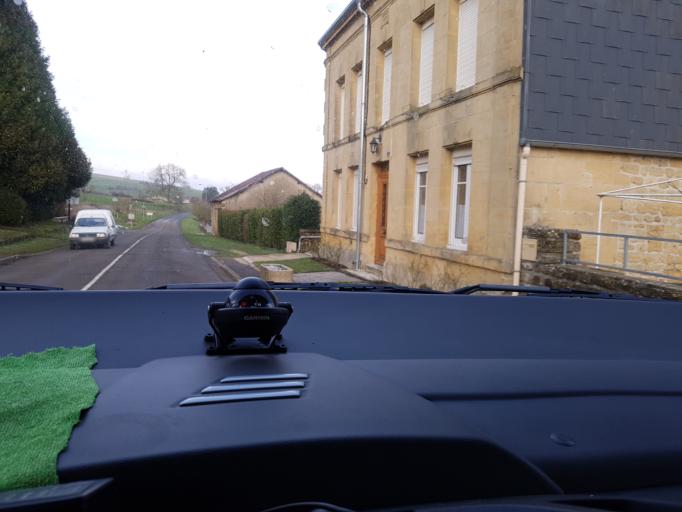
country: FR
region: Champagne-Ardenne
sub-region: Departement des Ardennes
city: Tournes
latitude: 49.7431
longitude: 4.5997
